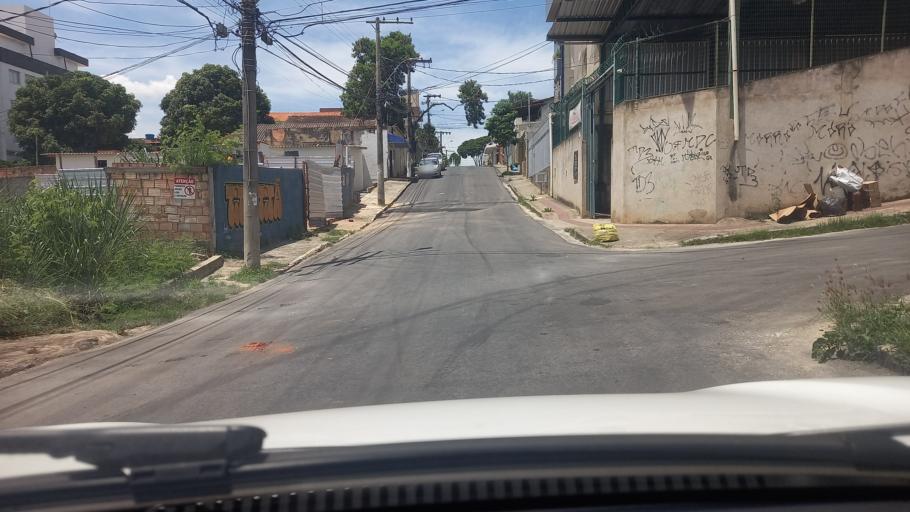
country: BR
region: Minas Gerais
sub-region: Belo Horizonte
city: Belo Horizonte
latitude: -19.9170
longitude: -43.9859
